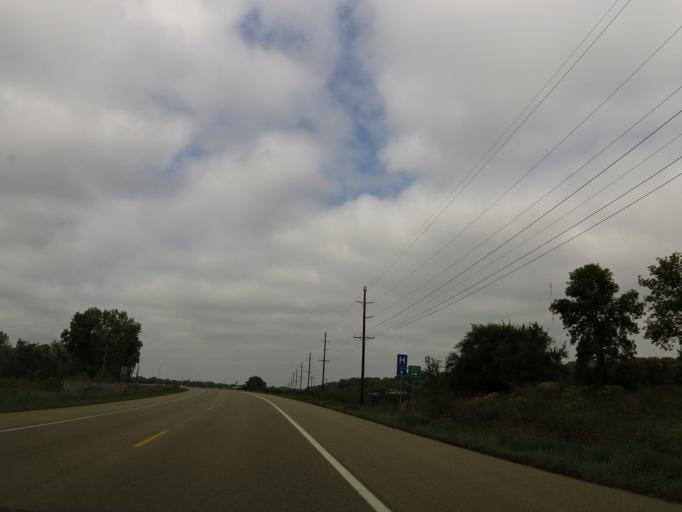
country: US
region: Minnesota
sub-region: Chippewa County
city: Montevideo
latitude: 44.9280
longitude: -95.7085
